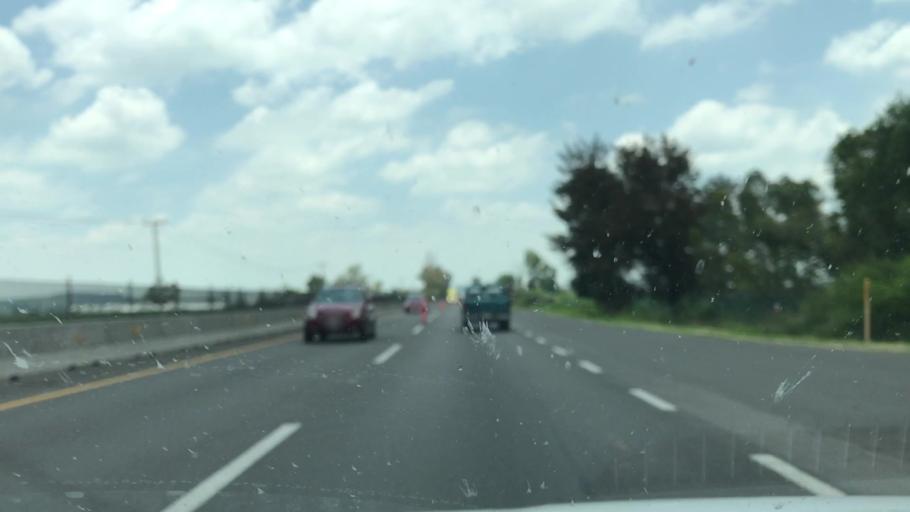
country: MX
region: Guanajuato
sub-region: Abasolo
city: San Bernardo Pena Blanca
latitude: 20.5010
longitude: -101.4789
